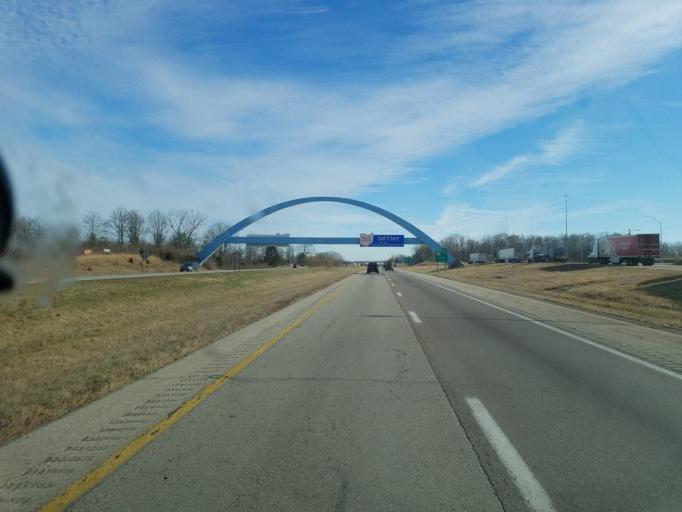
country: US
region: Ohio
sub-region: Preble County
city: New Paris
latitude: 39.8285
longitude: -84.8042
